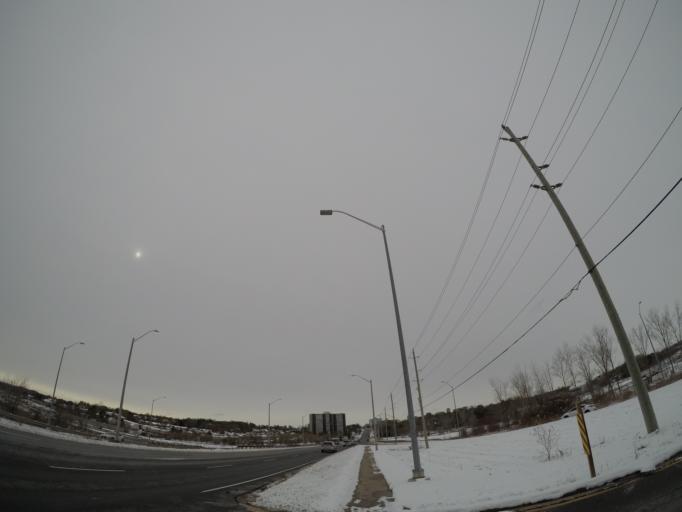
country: CA
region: Ontario
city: Waterloo
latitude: 43.4869
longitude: -80.4988
